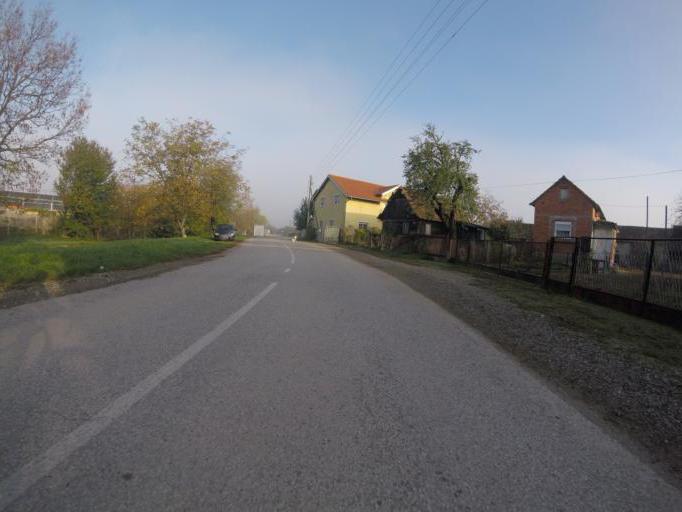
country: HR
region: Zagrebacka
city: Micevec
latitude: 45.7571
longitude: 16.0863
